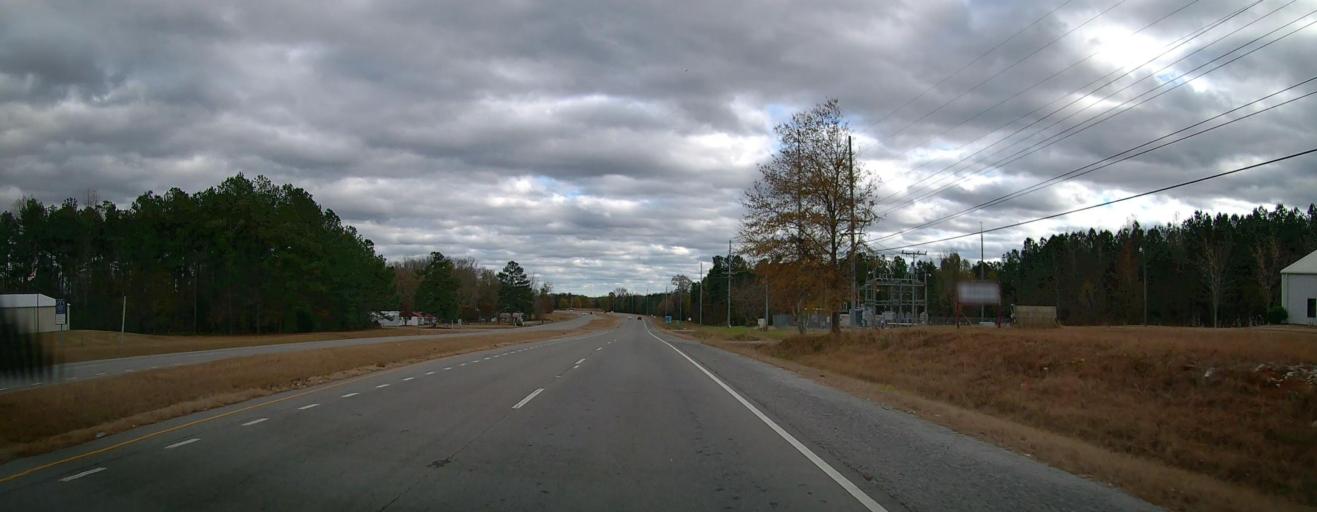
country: US
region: Alabama
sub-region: Lawrence County
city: Town Creek
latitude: 34.5779
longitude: -87.4059
